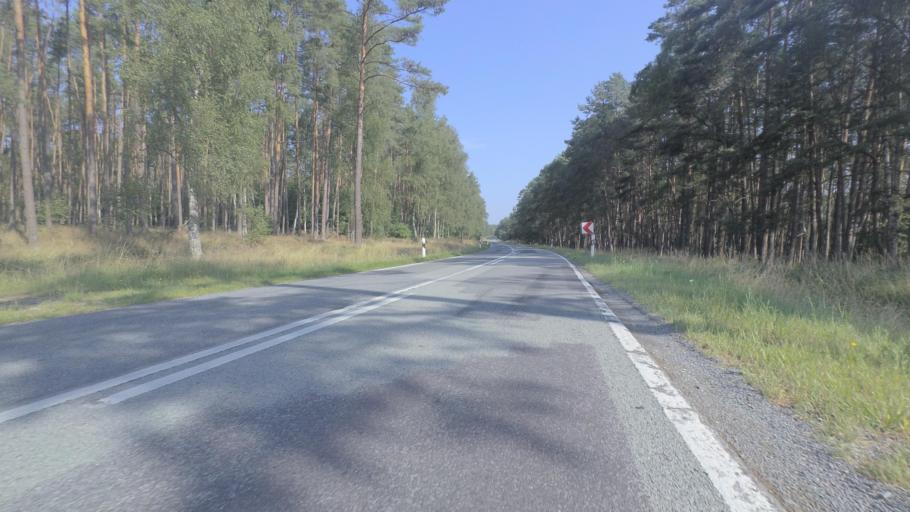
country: DE
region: Mecklenburg-Vorpommern
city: Malchow
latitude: 53.5596
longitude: 12.4534
